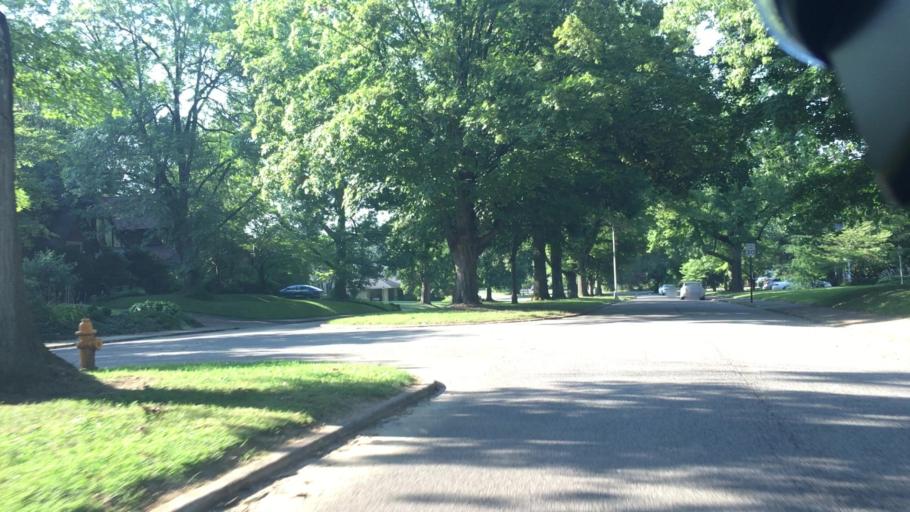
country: US
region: Indiana
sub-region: Vanderburgh County
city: Evansville
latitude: 37.9716
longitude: -87.5244
